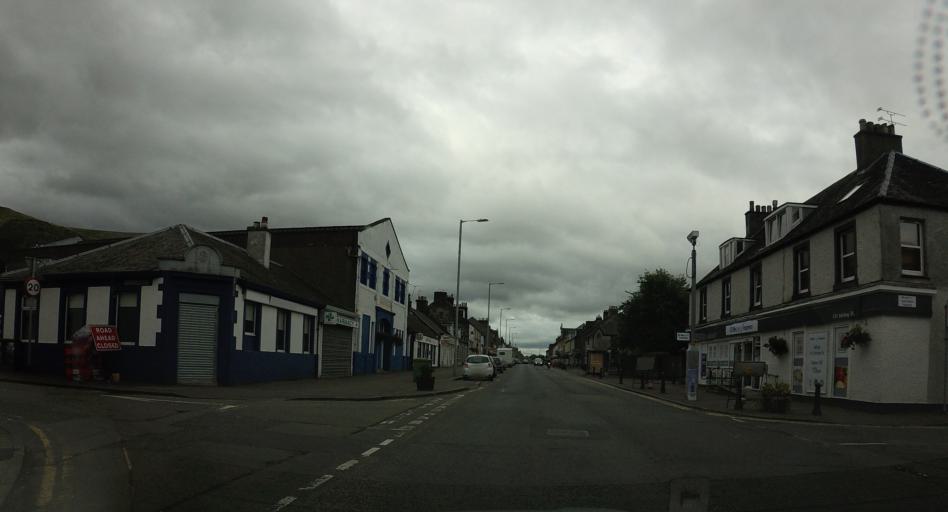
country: GB
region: Scotland
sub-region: Clackmannanshire
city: Alva
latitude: 56.1530
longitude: -3.8028
